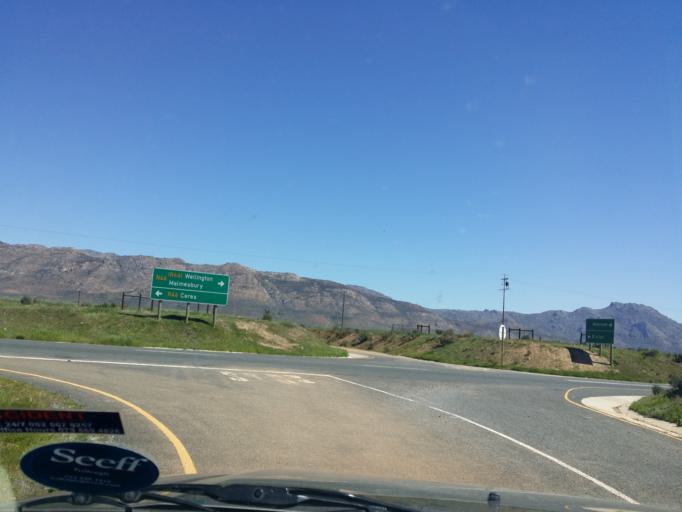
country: ZA
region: Western Cape
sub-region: Cape Winelands District Municipality
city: Ceres
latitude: -33.3635
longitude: 19.1706
